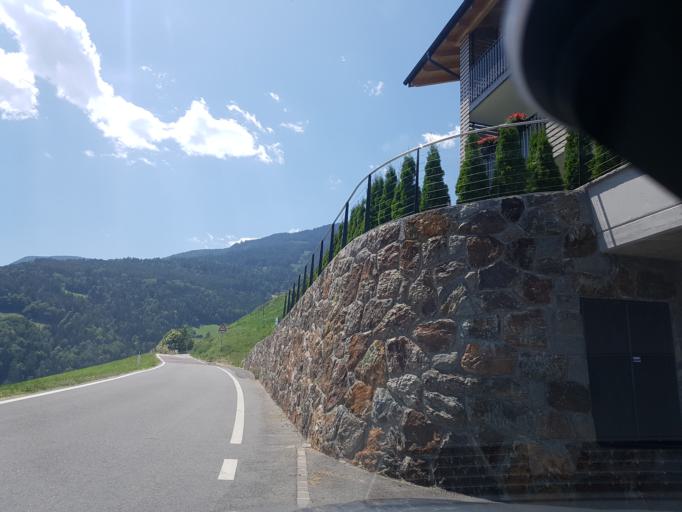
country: IT
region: Trentino-Alto Adige
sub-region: Bolzano
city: Villandro - Villanders
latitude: 46.6234
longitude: 11.5305
